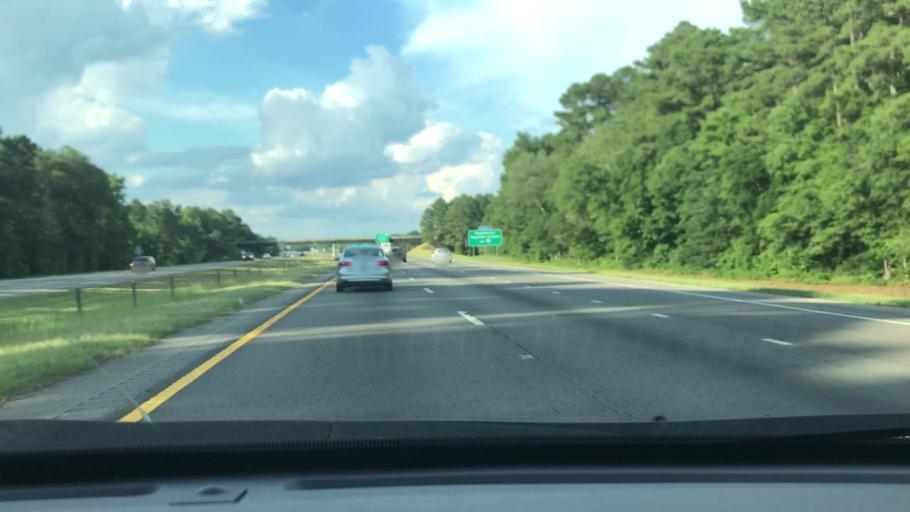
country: US
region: North Carolina
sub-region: Cumberland County
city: Hope Mills
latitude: 34.9187
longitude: -78.9490
